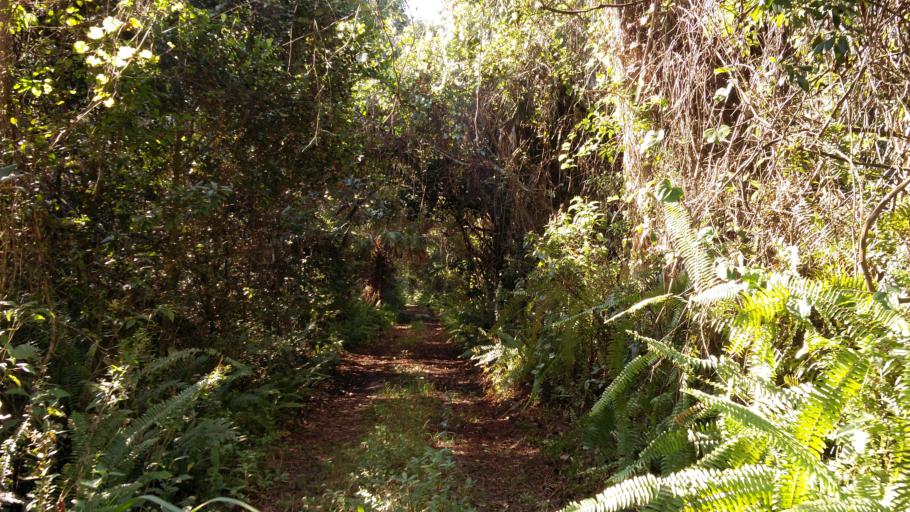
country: US
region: Florida
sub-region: Collier County
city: Lely Resort
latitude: 25.9796
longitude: -81.4232
